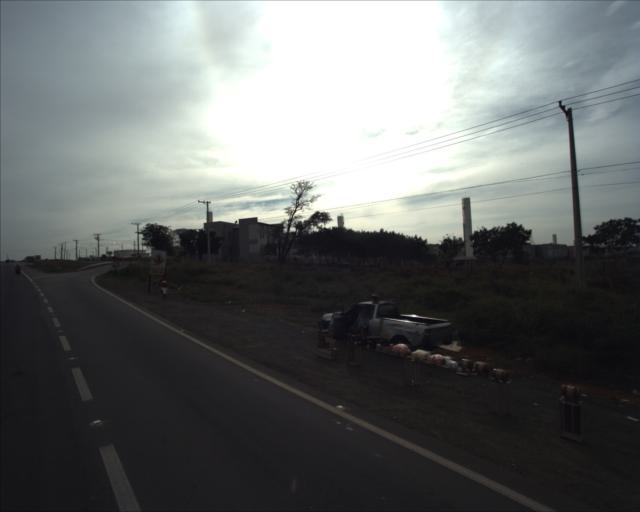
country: BR
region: Sao Paulo
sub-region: Sorocaba
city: Sorocaba
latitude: -23.4223
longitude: -47.5191
